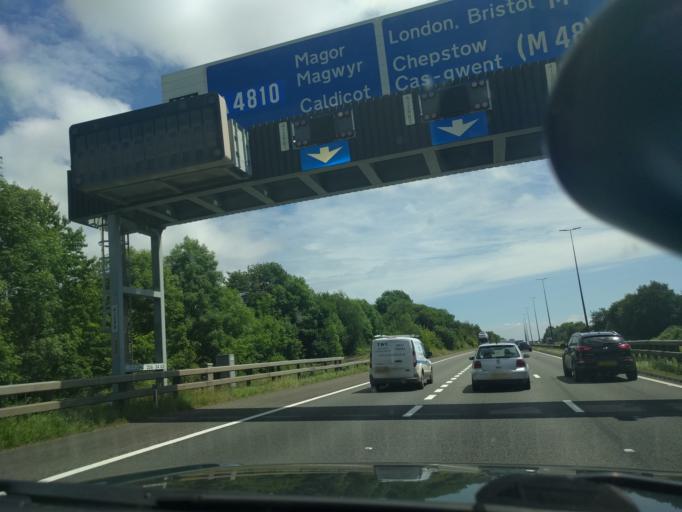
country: GB
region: Wales
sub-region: Newport
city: Bishton
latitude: 51.5928
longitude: -2.8562
